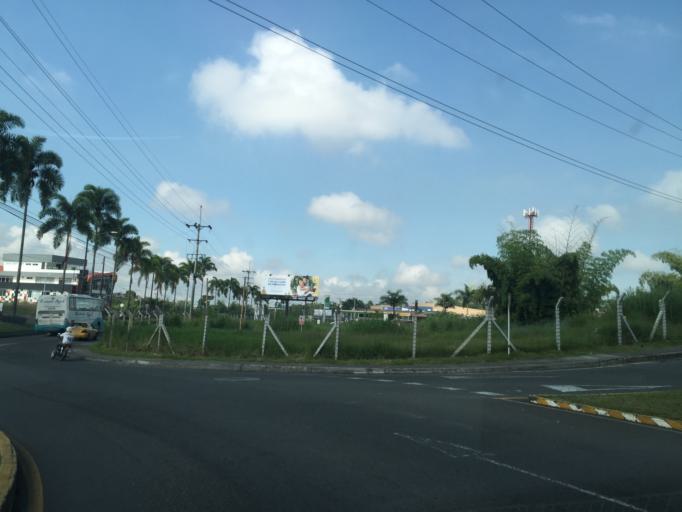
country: CO
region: Risaralda
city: Pereira
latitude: 4.8075
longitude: -75.7235
